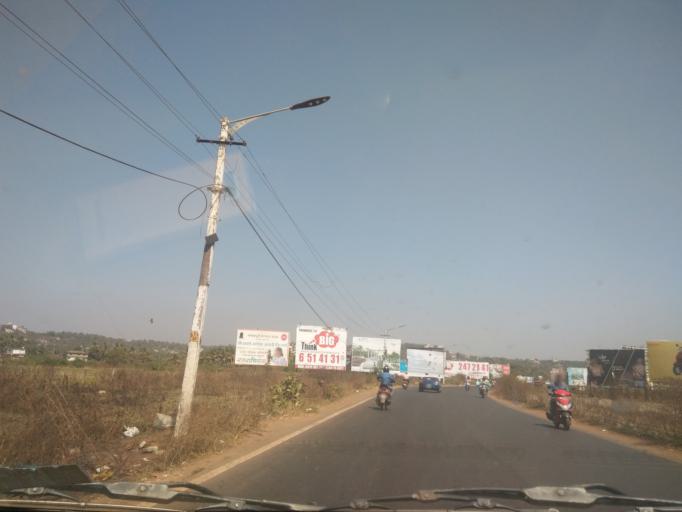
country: IN
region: Goa
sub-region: North Goa
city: Guirim
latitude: 15.5811
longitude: 73.8064
